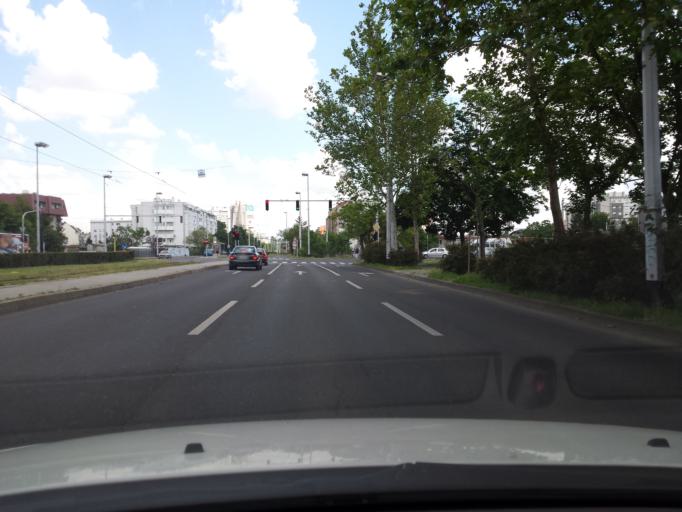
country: HR
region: Grad Zagreb
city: Novi Zagreb
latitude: 45.8028
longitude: 16.0140
